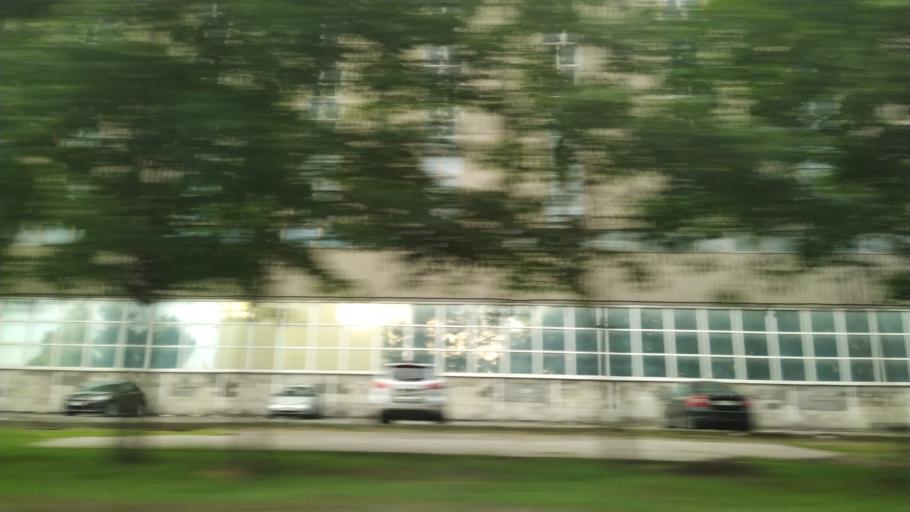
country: RU
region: Leningrad
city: Finlyandskiy
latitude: 59.9601
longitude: 30.3956
